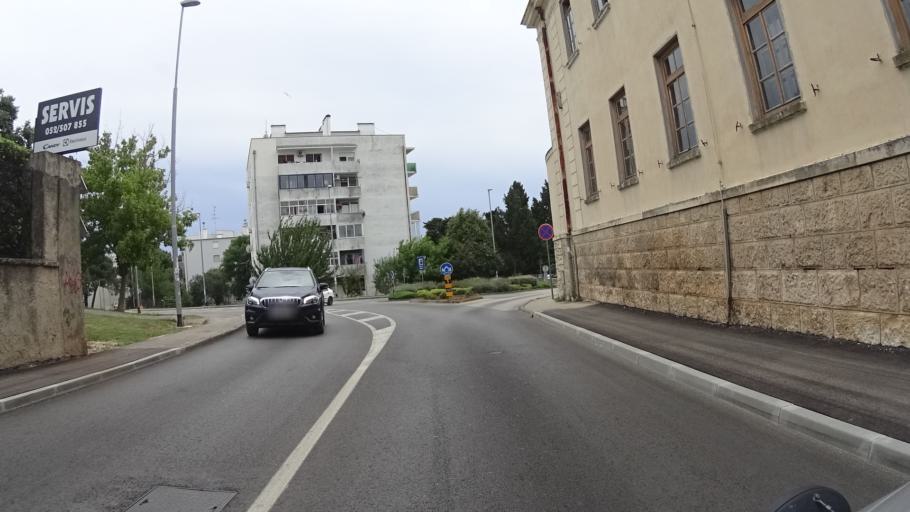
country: HR
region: Istarska
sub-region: Grad Pula
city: Pula
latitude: 44.8577
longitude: 13.8441
